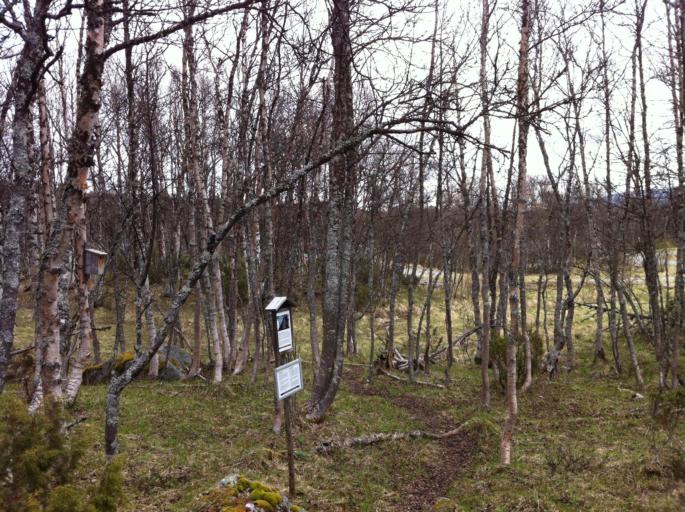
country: NO
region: Sor-Trondelag
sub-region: Tydal
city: Aas
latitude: 62.5536
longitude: 12.3143
